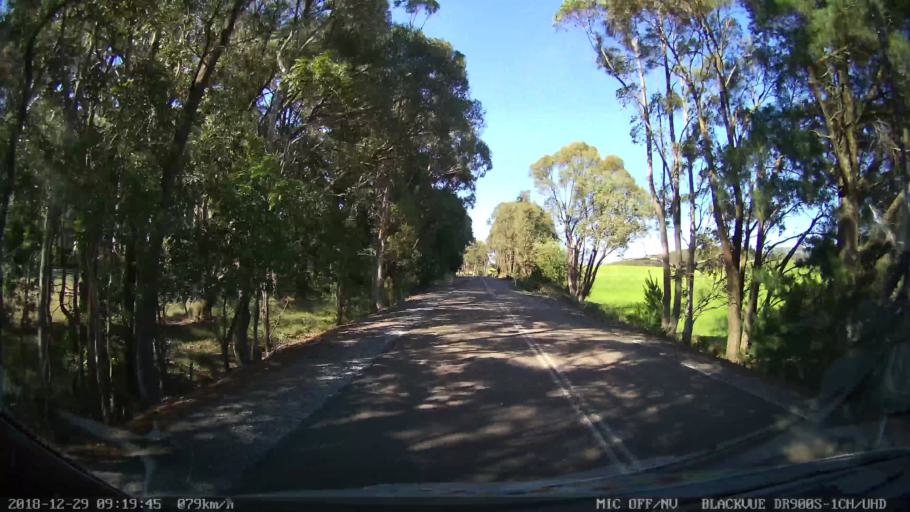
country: AU
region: New South Wales
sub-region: Upper Lachlan Shire
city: Crookwell
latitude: -34.4846
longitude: 149.4268
